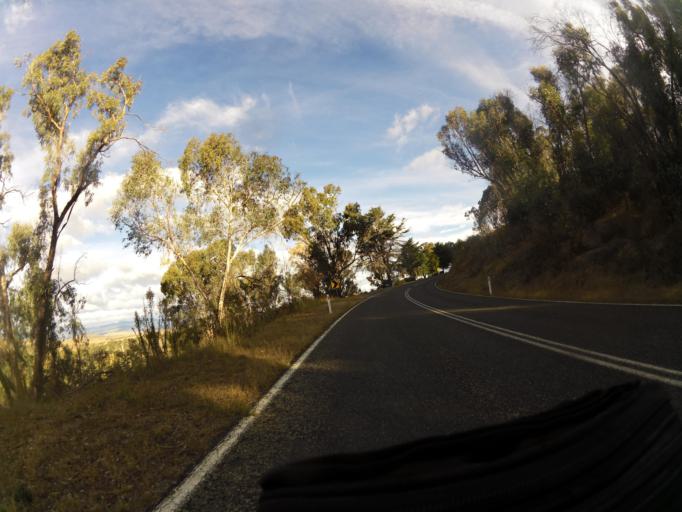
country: AU
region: New South Wales
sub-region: Greater Hume Shire
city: Holbrook
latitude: -36.0102
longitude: 147.9079
